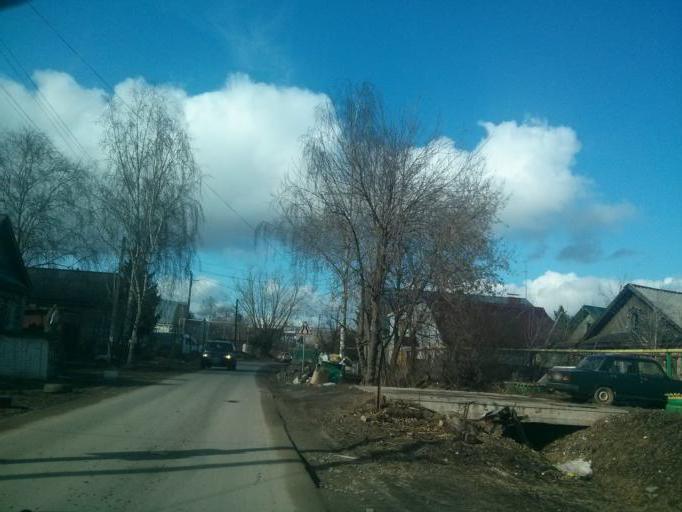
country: RU
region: Nizjnij Novgorod
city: Afonino
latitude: 56.2896
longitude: 44.1007
